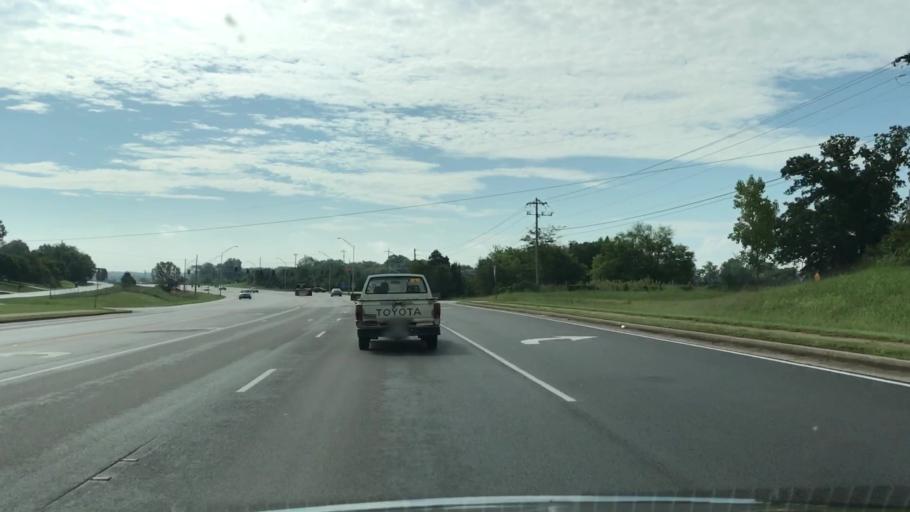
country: US
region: Kentucky
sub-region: Warren County
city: Plano
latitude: 36.9062
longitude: -86.4005
